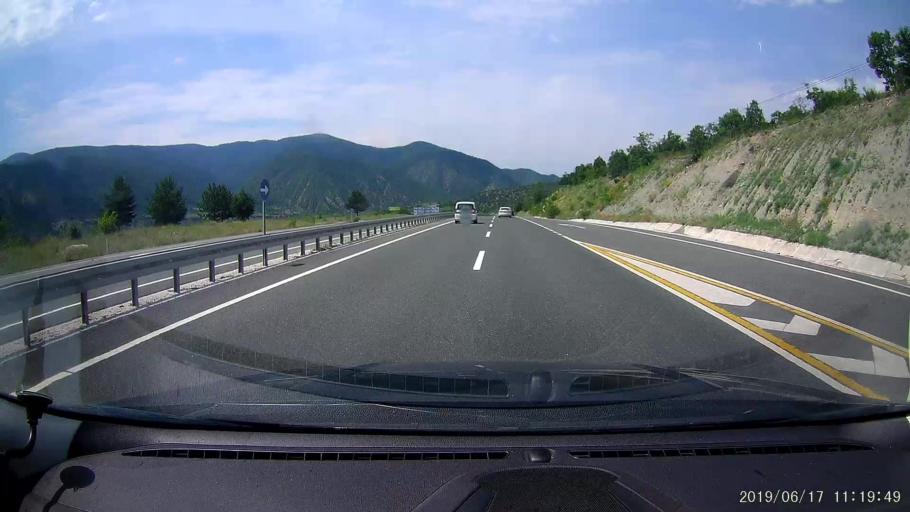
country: TR
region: Cankiri
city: Yaprakli
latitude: 40.9206
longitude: 33.8165
